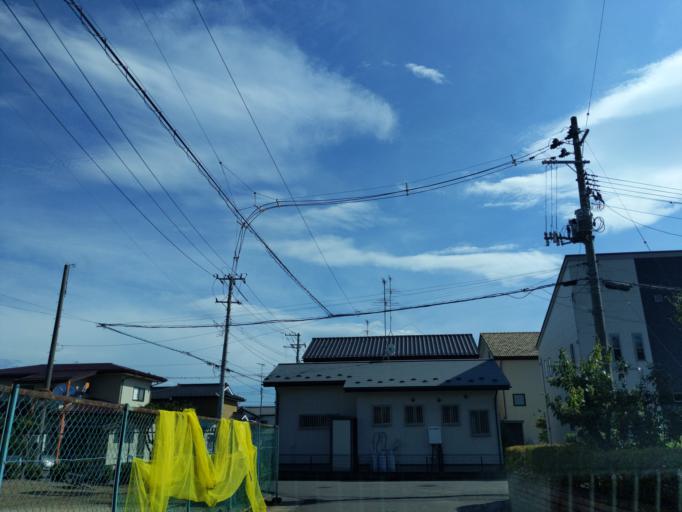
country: JP
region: Fukushima
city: Koriyama
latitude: 37.4076
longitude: 140.3293
